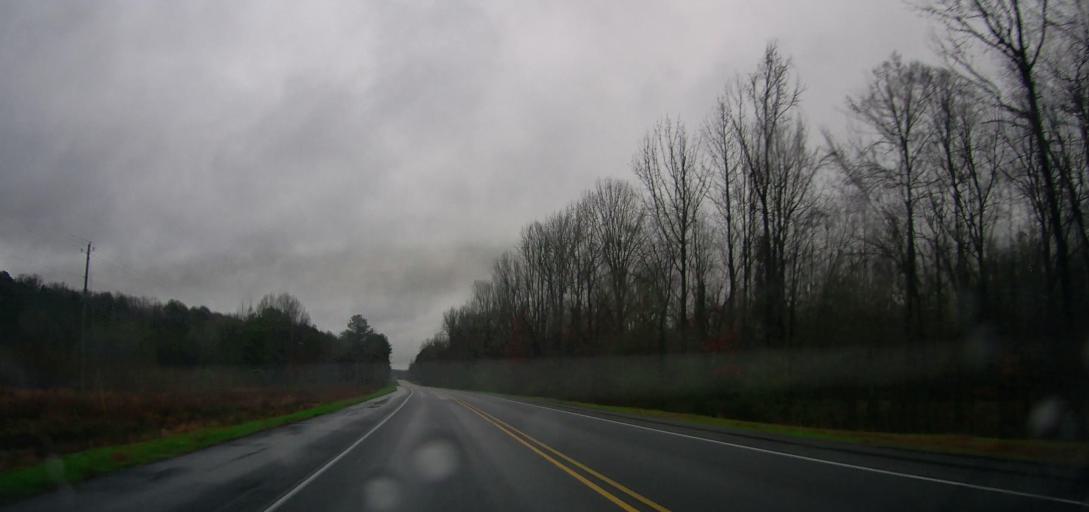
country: US
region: Alabama
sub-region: Bibb County
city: Centreville
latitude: 32.9299
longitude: -87.0528
